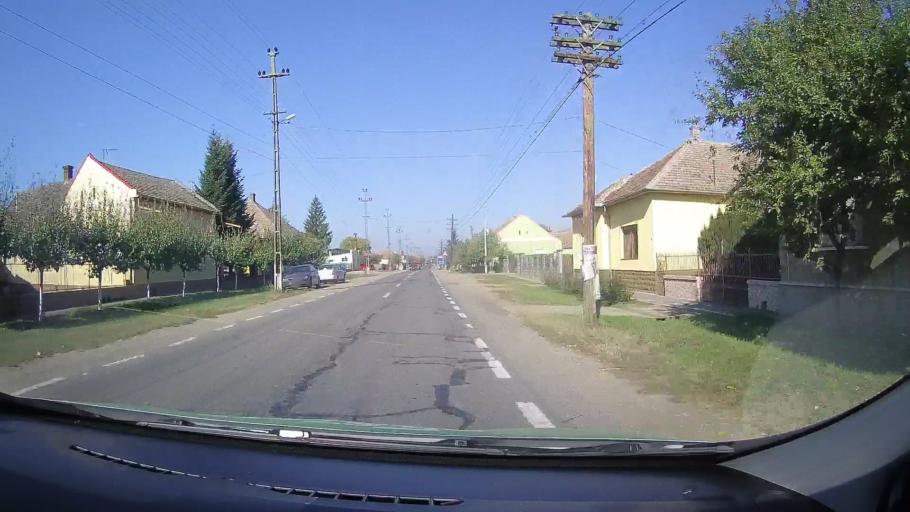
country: RO
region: Satu Mare
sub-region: Comuna Urziceni
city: Urziceni
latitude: 47.7298
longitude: 22.4059
